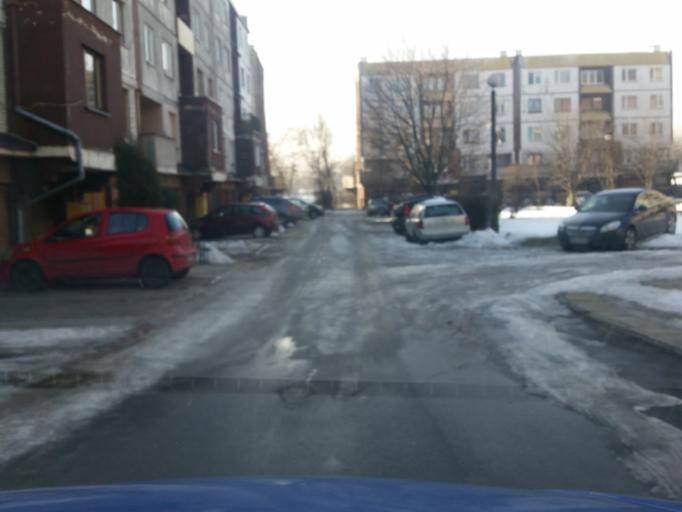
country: PL
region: Silesian Voivodeship
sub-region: Sosnowiec
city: Sosnowiec
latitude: 50.2704
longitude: 19.1182
